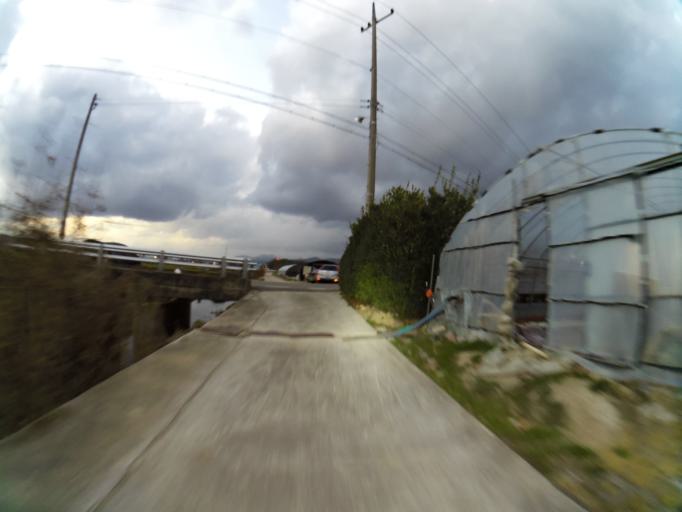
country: KR
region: Gyeongsangbuk-do
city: Gyeongsan-si
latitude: 35.8369
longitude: 128.7497
